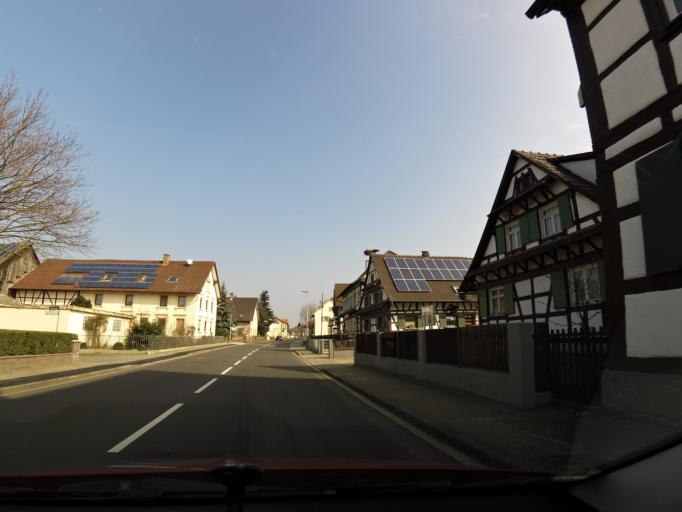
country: DE
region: Baden-Wuerttemberg
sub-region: Freiburg Region
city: Rheinau
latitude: 48.6241
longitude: 7.8937
